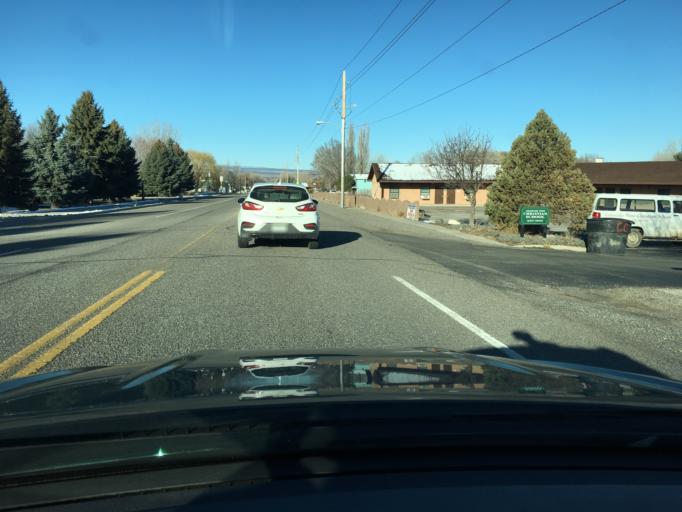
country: US
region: Colorado
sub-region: Montrose County
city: Montrose
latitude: 38.4745
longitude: -107.8447
